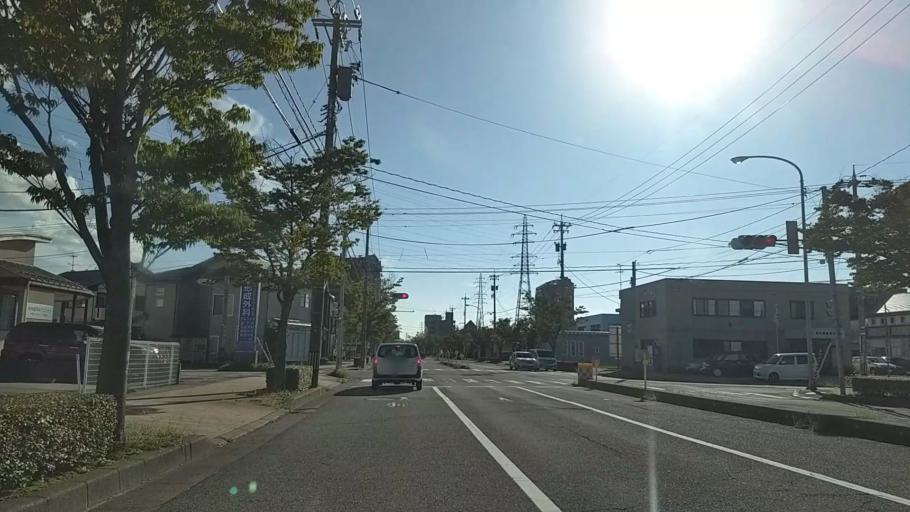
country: JP
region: Ishikawa
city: Kanazawa-shi
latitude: 36.5878
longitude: 136.6406
